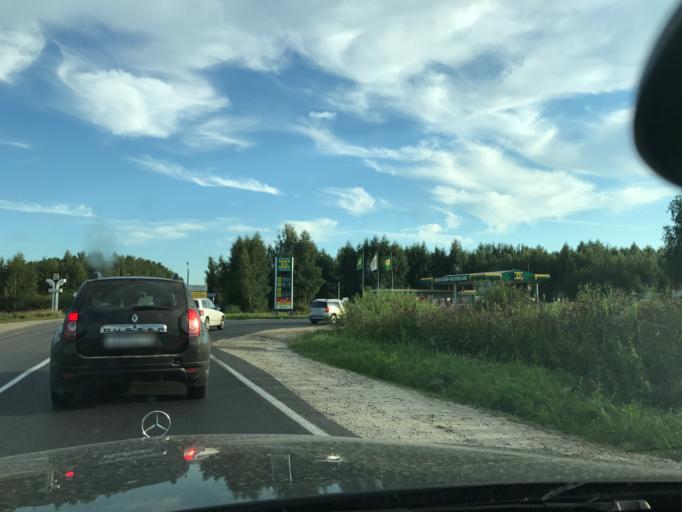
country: RU
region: Vladimir
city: Raduzhnyy
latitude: 56.0074
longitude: 40.3066
